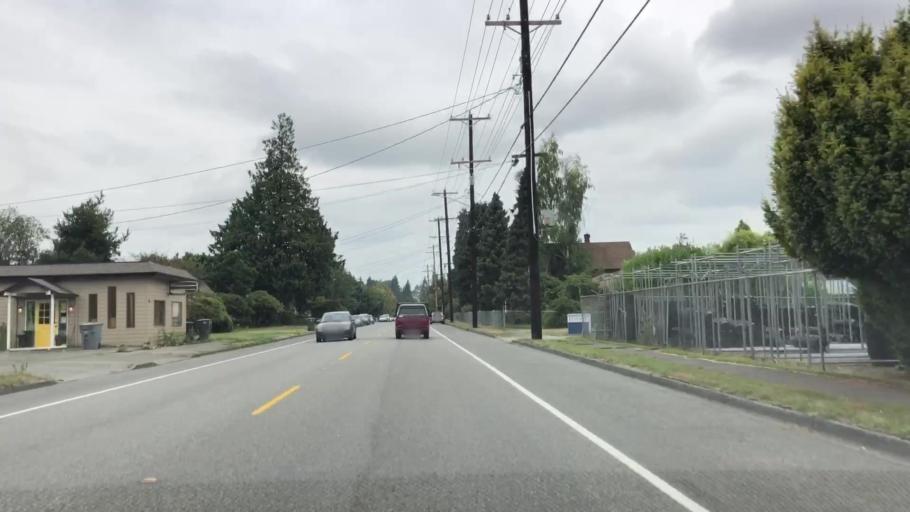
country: US
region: Washington
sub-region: Snohomish County
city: Snohomish
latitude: 47.9142
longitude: -122.0860
